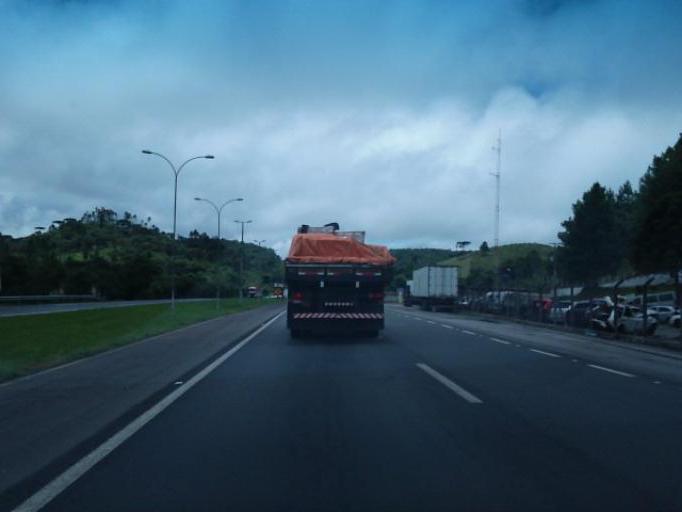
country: BR
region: Parana
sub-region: Campina Grande Do Sul
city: Campina Grande do Sul
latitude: -25.2811
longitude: -48.9271
